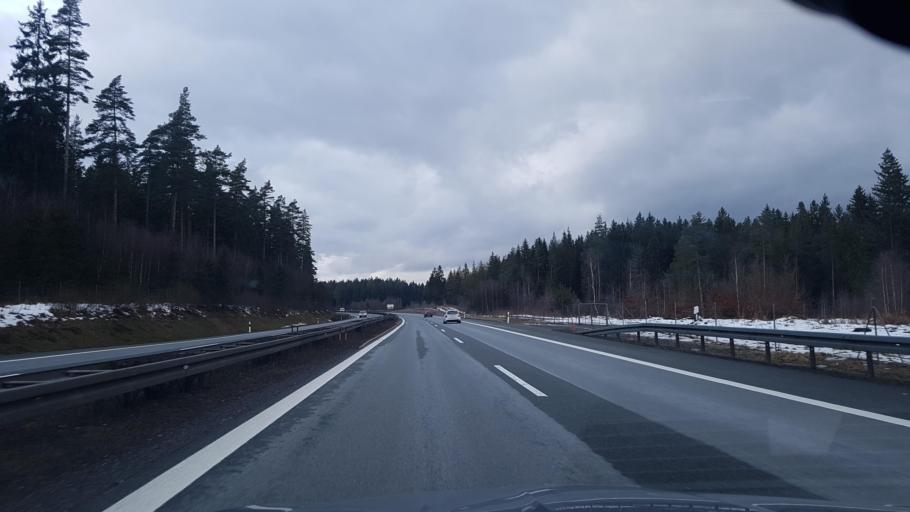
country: DE
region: Bavaria
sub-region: Upper Franconia
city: Schonwald
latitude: 50.2216
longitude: 12.0790
